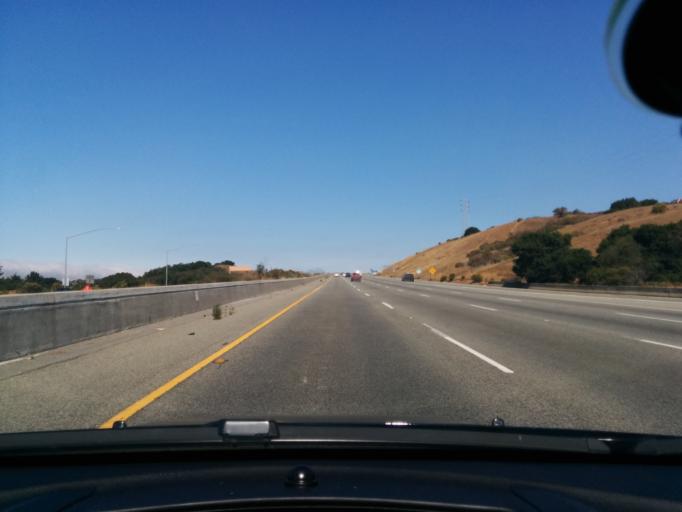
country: US
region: California
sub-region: San Mateo County
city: Emerald Lake Hills
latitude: 37.4707
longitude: -122.2940
